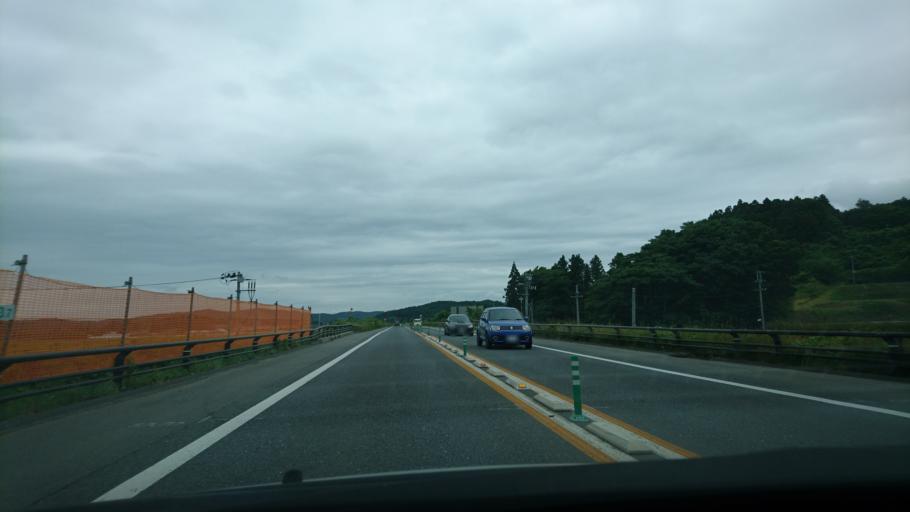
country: JP
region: Miyagi
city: Wakuya
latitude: 38.5786
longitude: 141.2738
